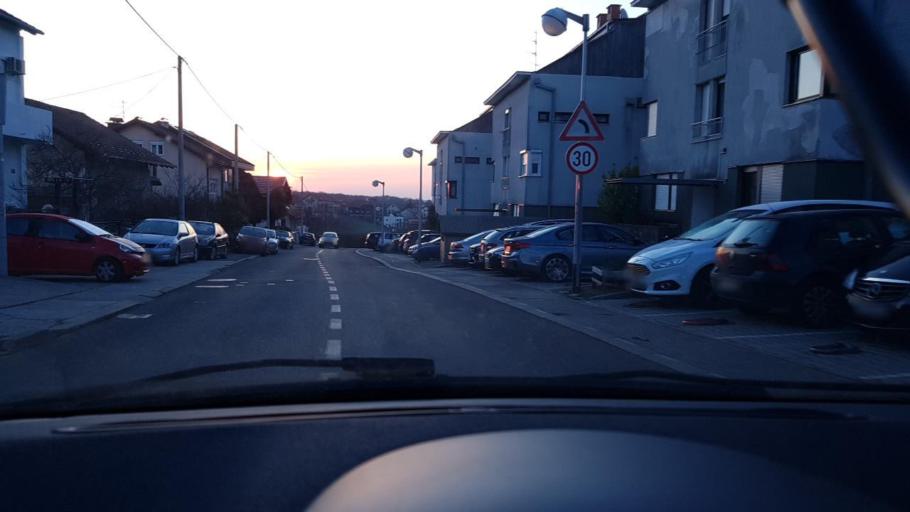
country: HR
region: Grad Zagreb
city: Zagreb
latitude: 45.8315
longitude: 16.0022
